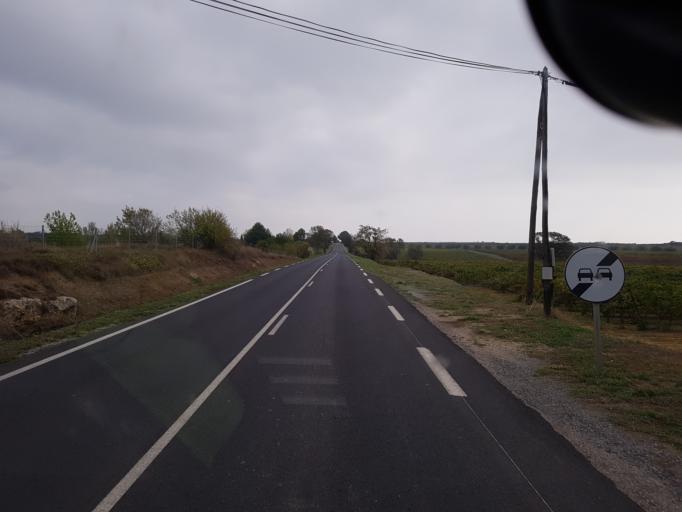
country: FR
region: Languedoc-Roussillon
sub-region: Departement de l'Herault
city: Meze
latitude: 43.4262
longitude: 3.5567
